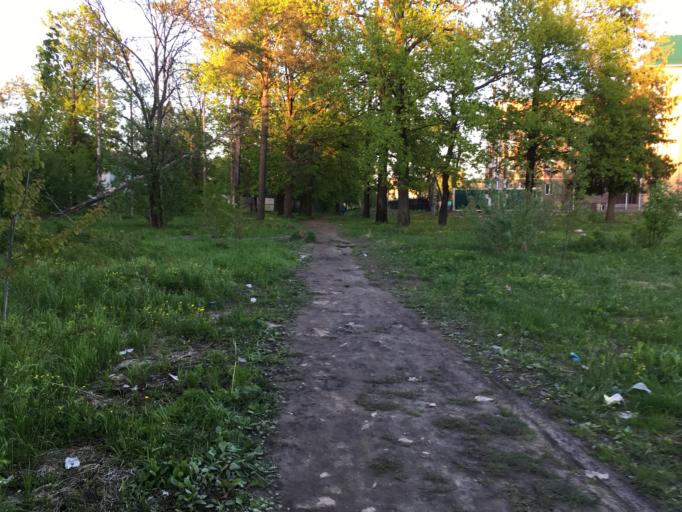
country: RU
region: Mariy-El
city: Yoshkar-Ola
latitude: 56.6298
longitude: 47.9342
